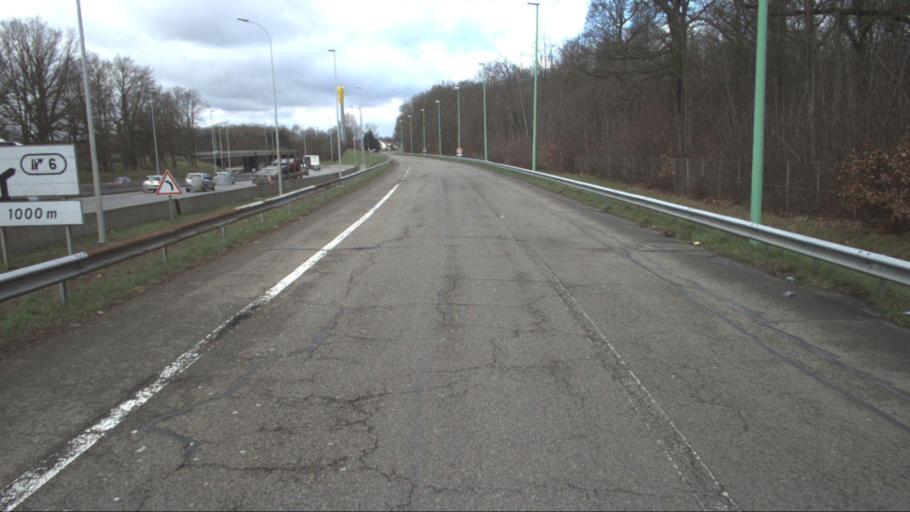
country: FR
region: Ile-de-France
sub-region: Departement des Yvelines
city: Saint-Cyr-l'Ecole
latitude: 48.7936
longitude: 2.0802
